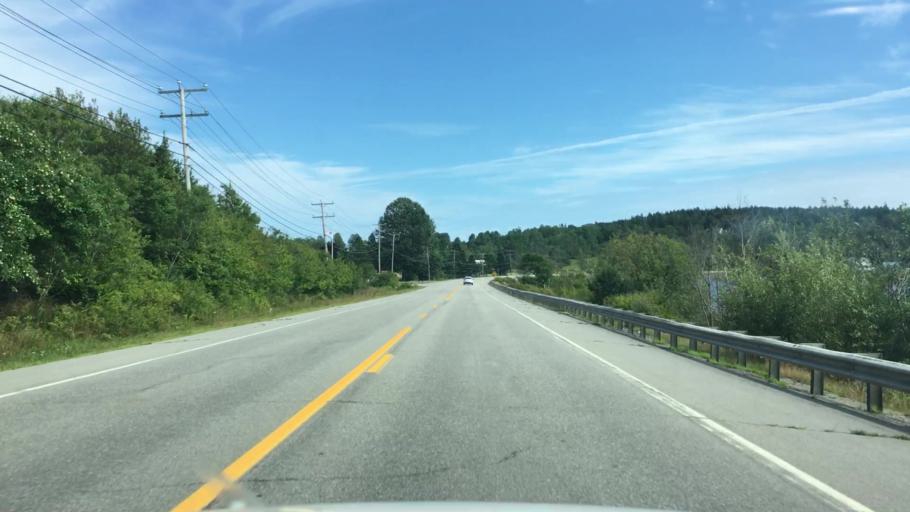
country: US
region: Maine
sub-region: Washington County
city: Eastport
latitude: 44.9259
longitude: -67.0203
